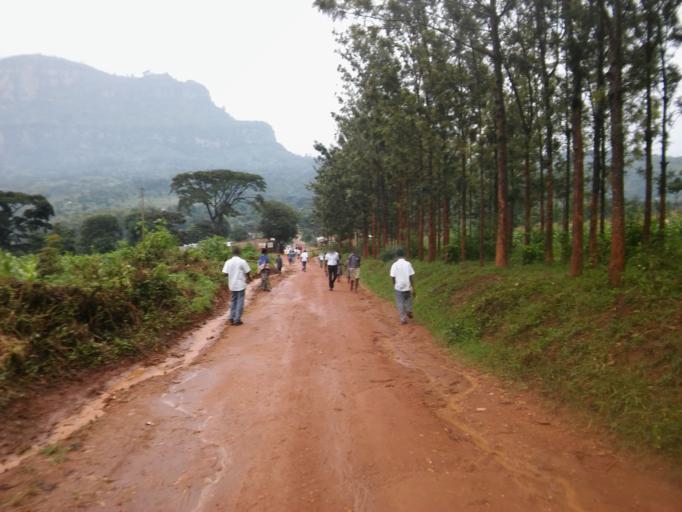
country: UG
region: Eastern Region
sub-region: Bududa District
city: Bududa
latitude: 0.9883
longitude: 34.2278
